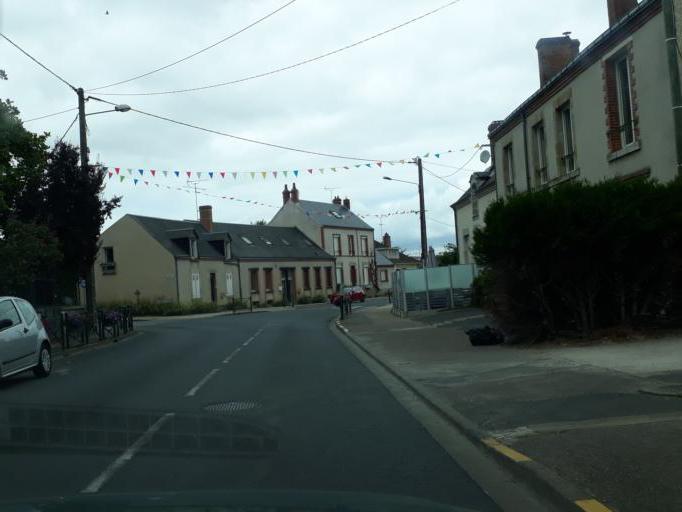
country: FR
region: Centre
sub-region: Departement du Loiret
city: Sandillon
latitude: 47.8460
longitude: 2.0286
